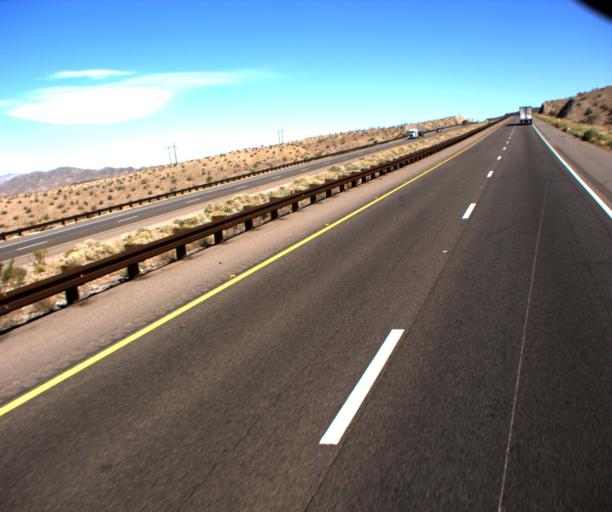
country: US
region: Nevada
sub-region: Clark County
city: Boulder City
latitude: 35.9212
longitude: -114.6314
